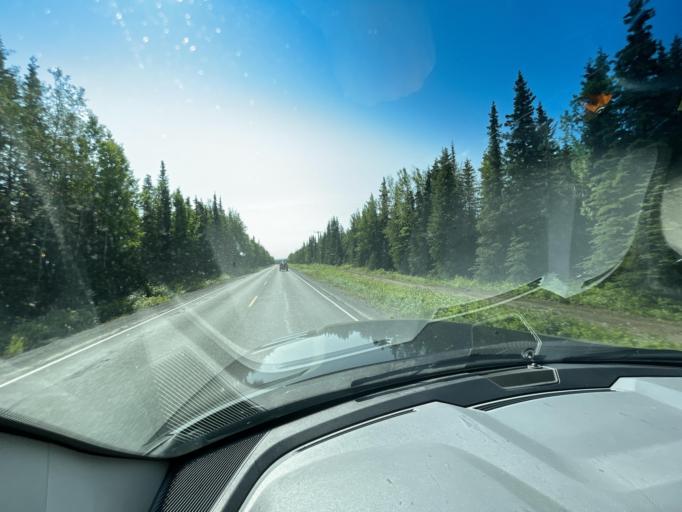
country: US
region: Alaska
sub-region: Kenai Peninsula Borough
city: Cohoe
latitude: 60.3081
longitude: -151.2894
